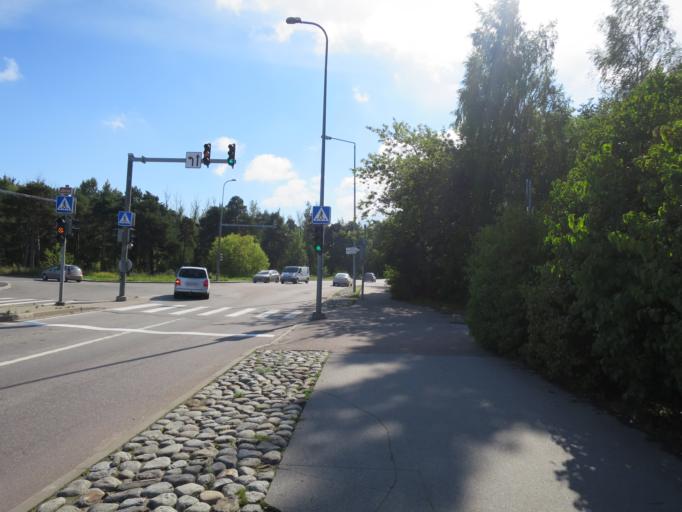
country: EE
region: Harju
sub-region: Tallinna linn
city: Tallinn
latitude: 59.4011
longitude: 24.7109
